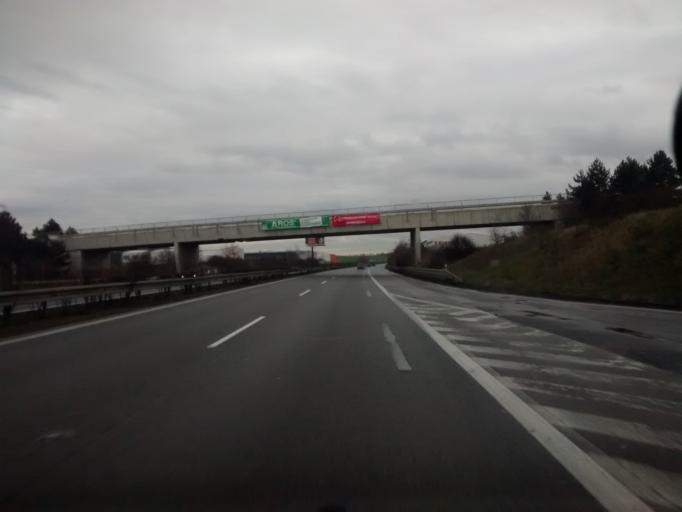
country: CZ
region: Central Bohemia
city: Odolena Voda
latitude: 50.2056
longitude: 14.4359
